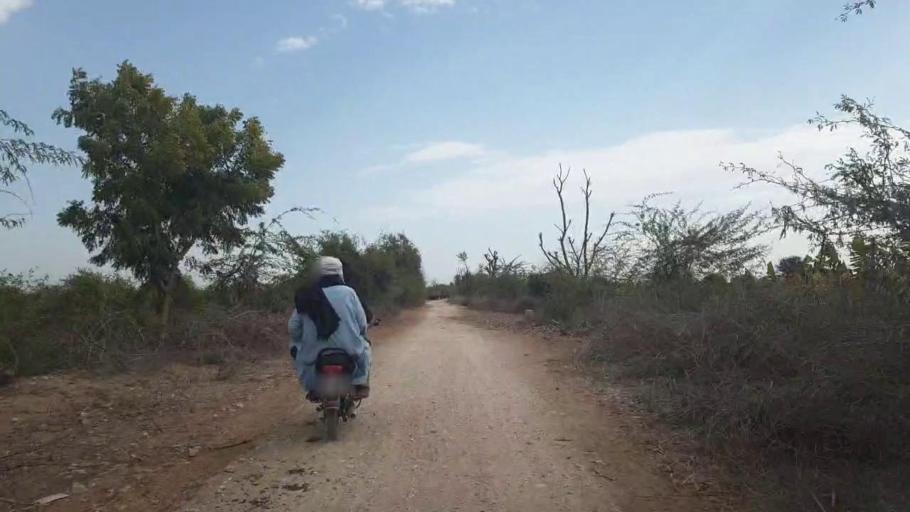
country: PK
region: Sindh
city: Sakrand
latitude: 25.9985
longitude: 68.3334
